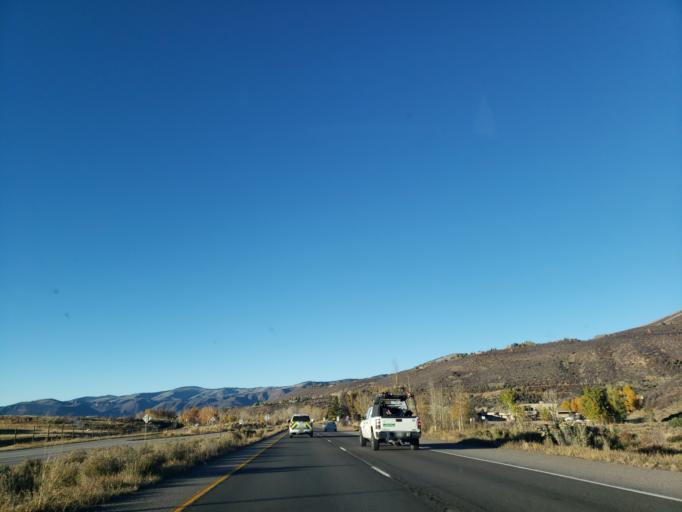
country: US
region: Colorado
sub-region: Pitkin County
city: Aspen
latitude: 39.2140
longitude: -106.8615
